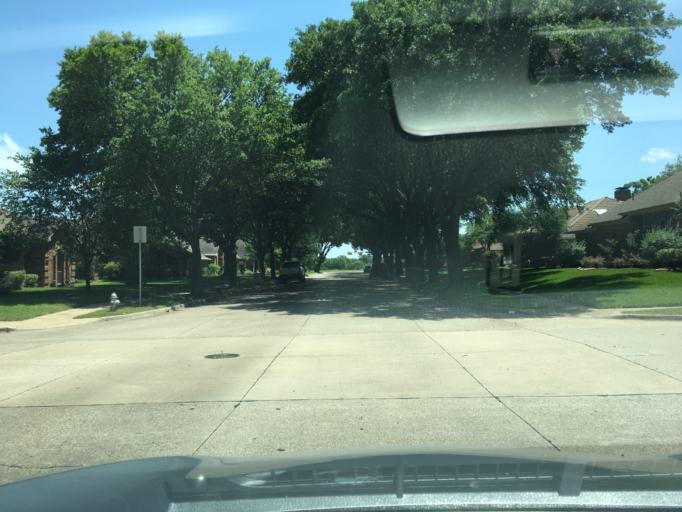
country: US
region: Texas
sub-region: Dallas County
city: Garland
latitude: 32.9327
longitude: -96.6757
